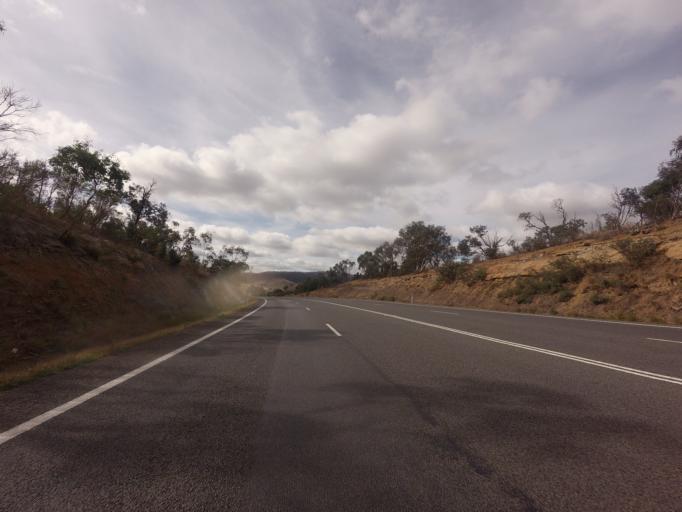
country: AU
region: Tasmania
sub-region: Brighton
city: Bridgewater
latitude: -42.4479
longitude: 147.2137
